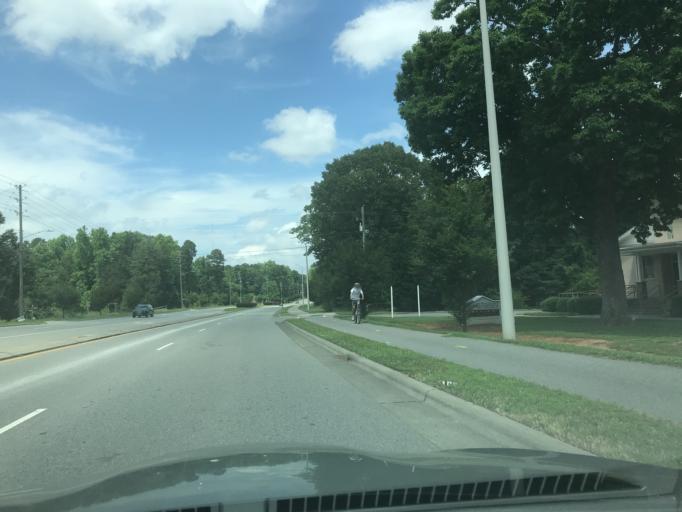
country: US
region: North Carolina
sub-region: Wake County
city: Wake Forest
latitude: 35.9195
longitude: -78.5925
